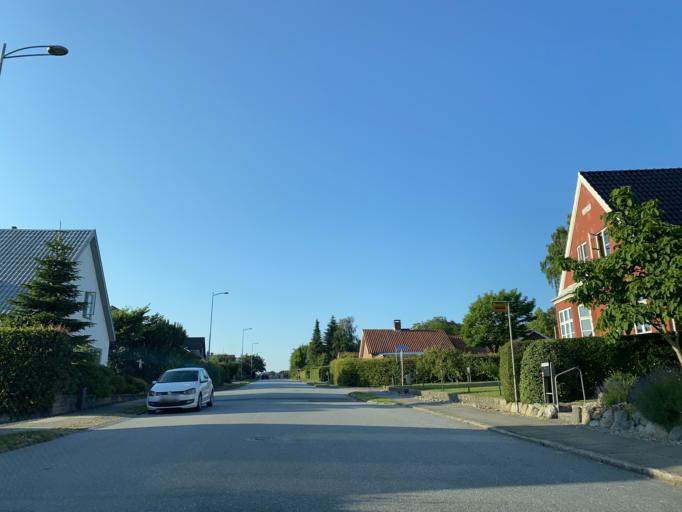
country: DK
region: South Denmark
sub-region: Aabenraa Kommune
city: Aabenraa
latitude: 55.0548
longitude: 9.4313
